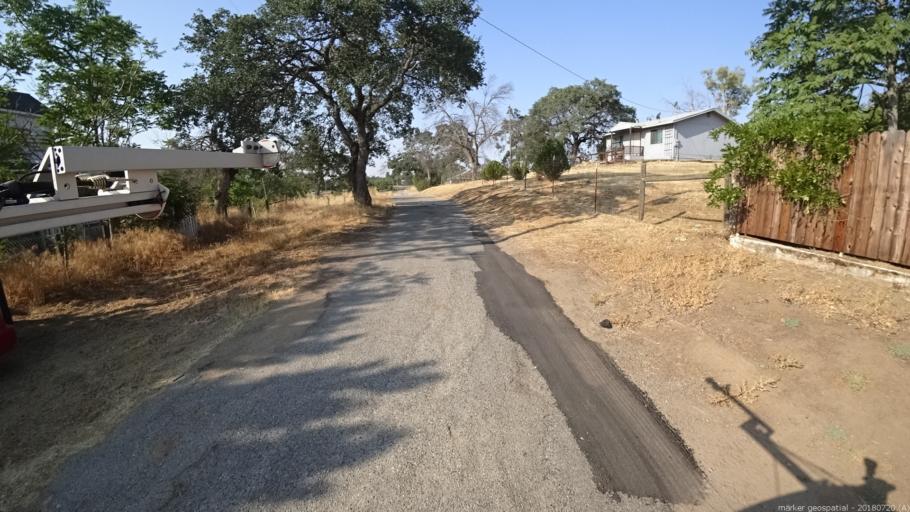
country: US
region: California
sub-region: Madera County
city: Yosemite Lakes
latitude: 37.2160
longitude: -119.9083
